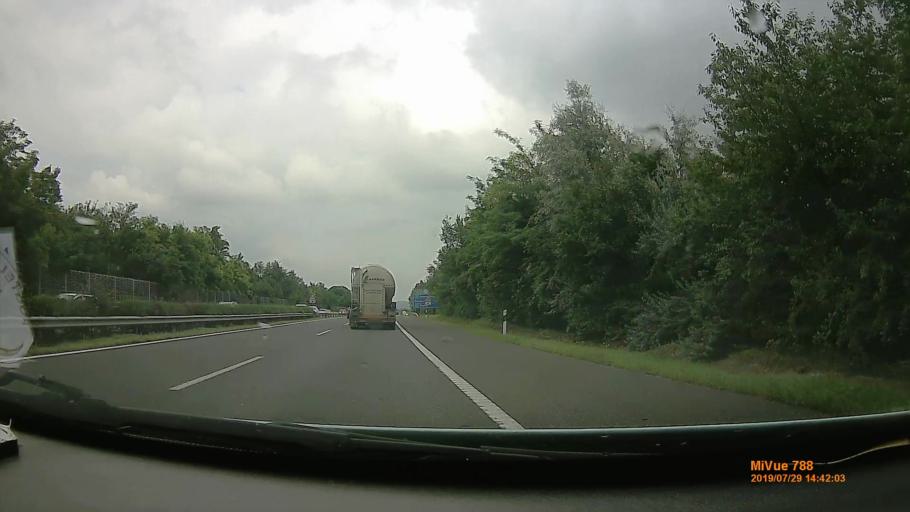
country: HU
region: Fejer
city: Lepseny
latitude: 46.9854
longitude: 18.1801
